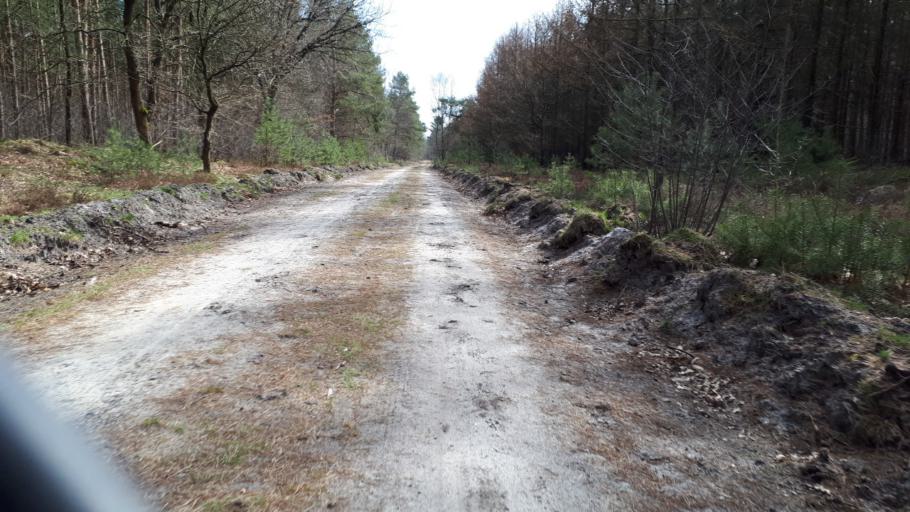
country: DE
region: Lower Saxony
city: Grossenkneten
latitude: 53.0302
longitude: 8.2865
